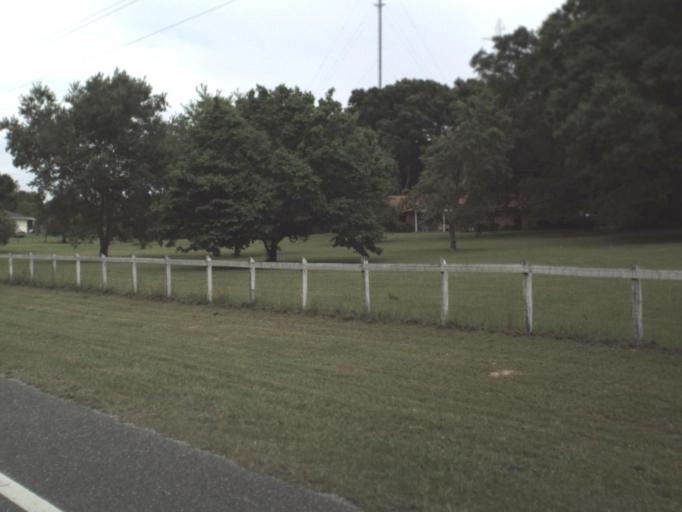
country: US
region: Florida
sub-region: Suwannee County
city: Wellborn
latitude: 30.0115
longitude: -82.8459
